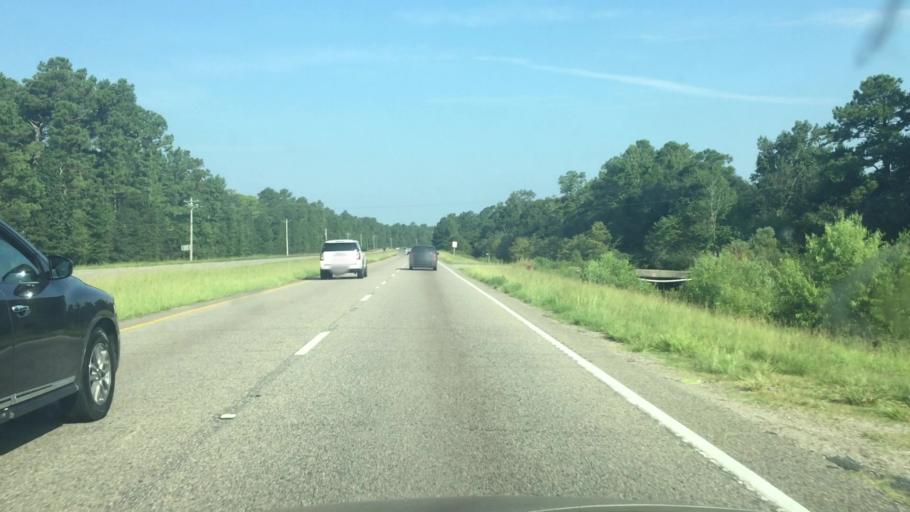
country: US
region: South Carolina
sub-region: Horry County
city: North Myrtle Beach
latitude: 33.9128
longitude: -78.7157
